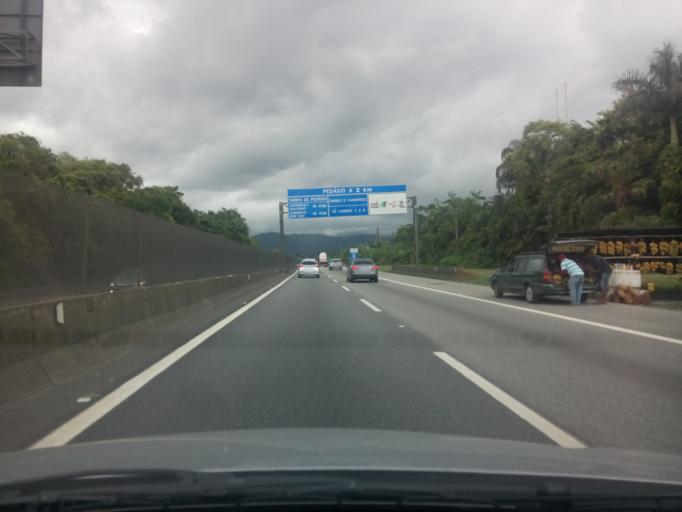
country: BR
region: Sao Paulo
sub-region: Santos
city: Santos
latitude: -23.9110
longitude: -46.2922
